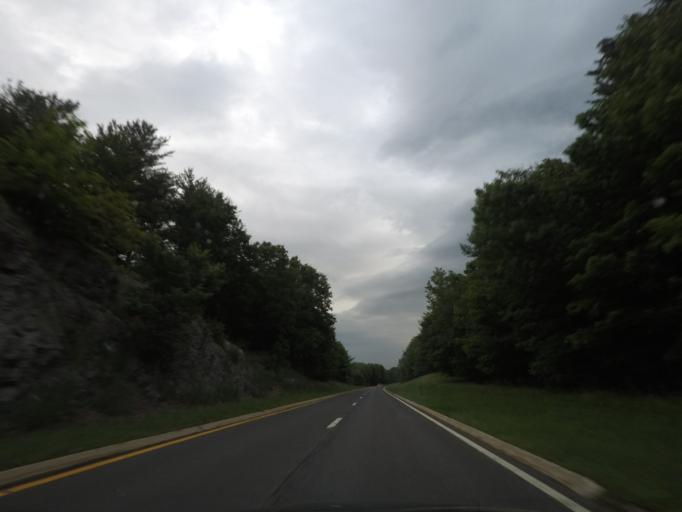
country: US
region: New York
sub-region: Columbia County
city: Philmont
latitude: 42.2411
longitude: -73.6215
